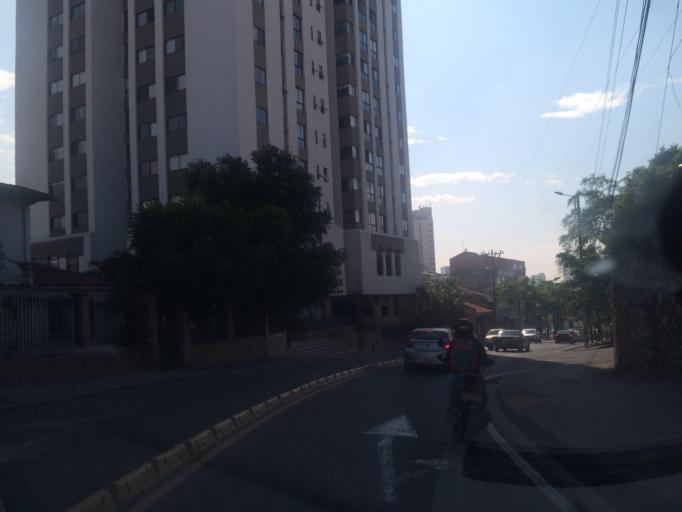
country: CO
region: Valle del Cauca
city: Cali
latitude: 3.4491
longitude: -76.5419
